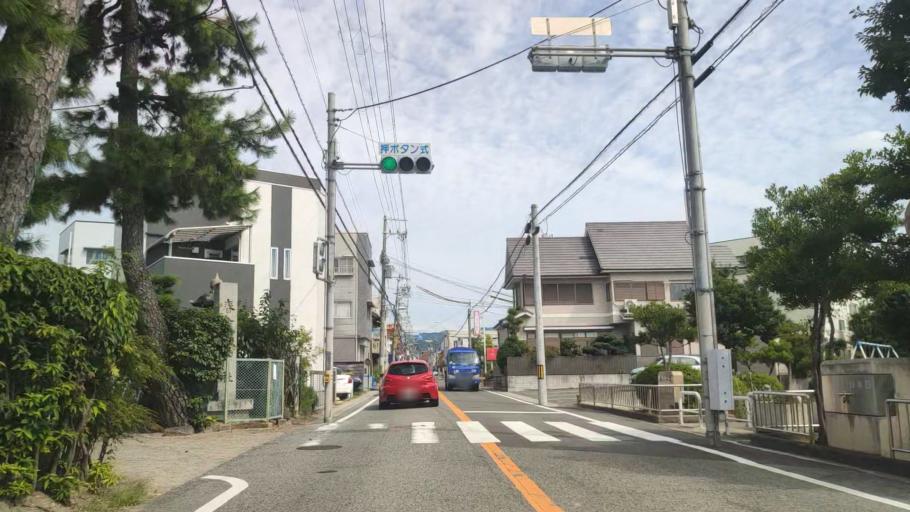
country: JP
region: Osaka
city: Mino
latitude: 34.8064
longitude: 135.4647
